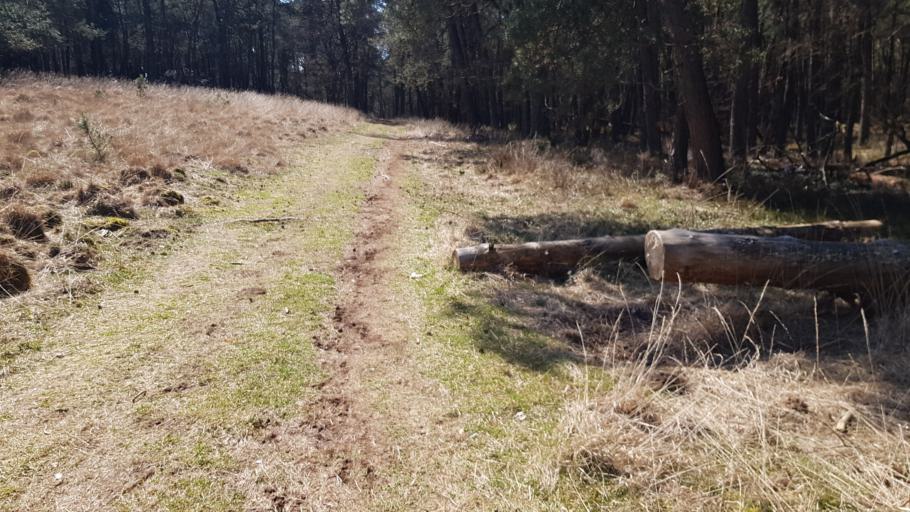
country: NL
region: Gelderland
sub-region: Gemeente Rozendaal
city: Rozendaal
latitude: 52.0579
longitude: 5.9907
